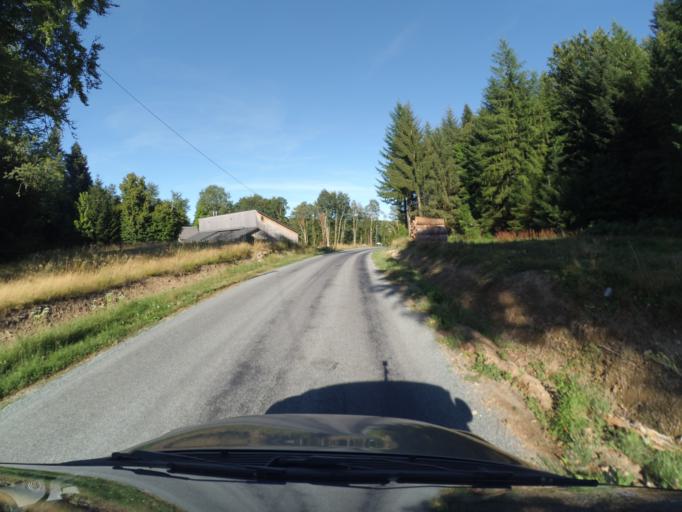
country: FR
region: Limousin
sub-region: Departement de la Creuse
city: Banize
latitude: 45.7839
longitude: 1.9862
